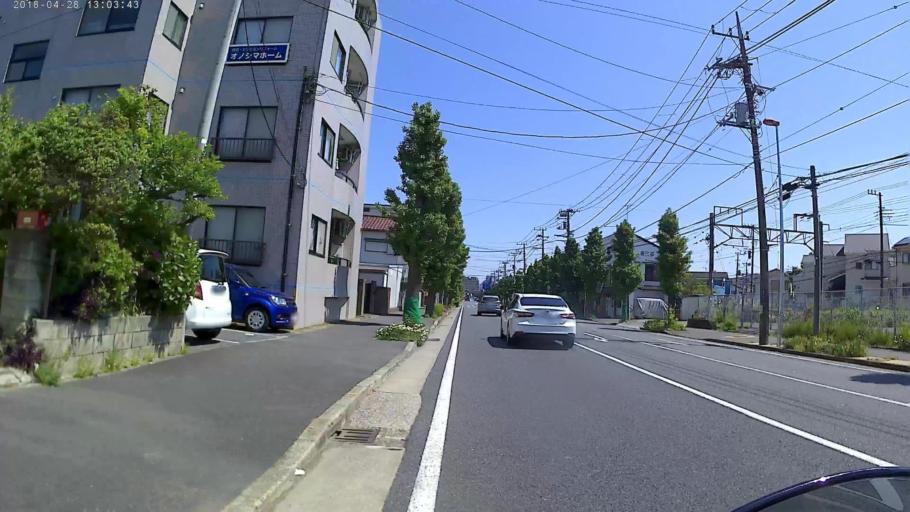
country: JP
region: Kanagawa
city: Yokosuka
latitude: 35.2506
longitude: 139.6795
